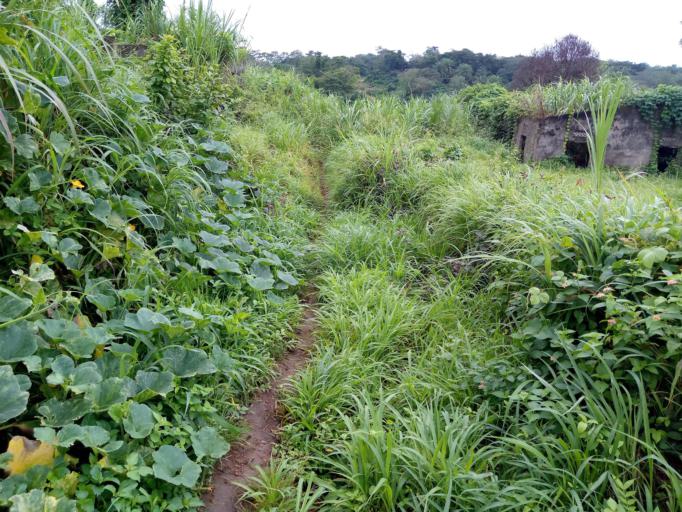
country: SL
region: Eastern Province
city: Buedu
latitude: 8.4637
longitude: -10.3370
